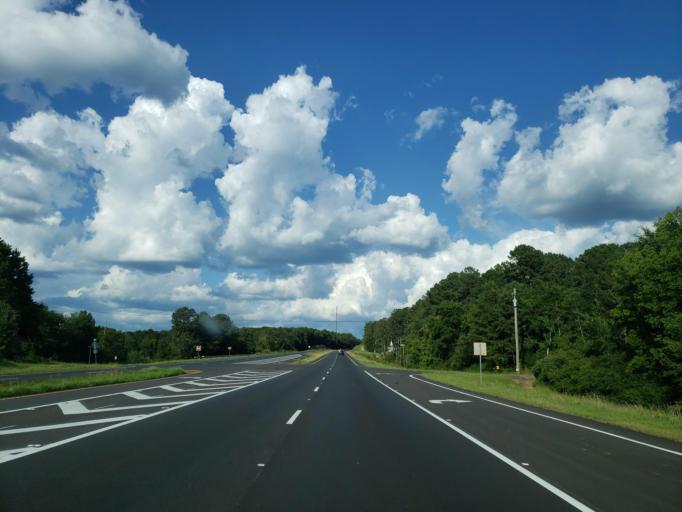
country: US
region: Georgia
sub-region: Floyd County
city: Rome
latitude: 34.2075
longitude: -85.0593
